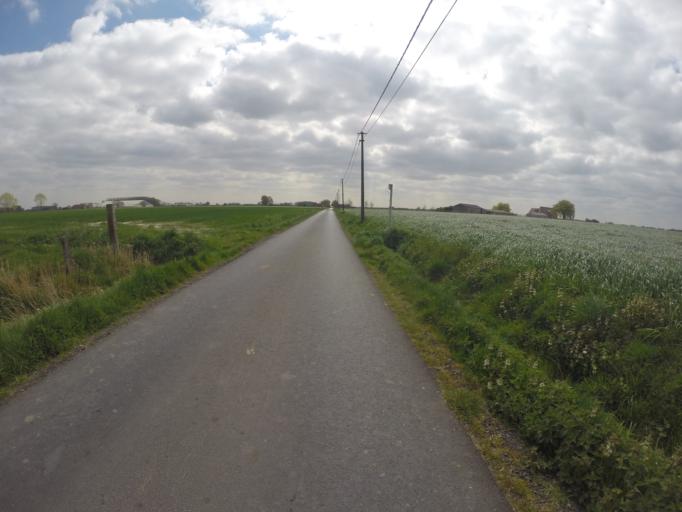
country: BE
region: Flanders
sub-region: Provincie Oost-Vlaanderen
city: Nevele
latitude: 51.0362
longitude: 3.4857
